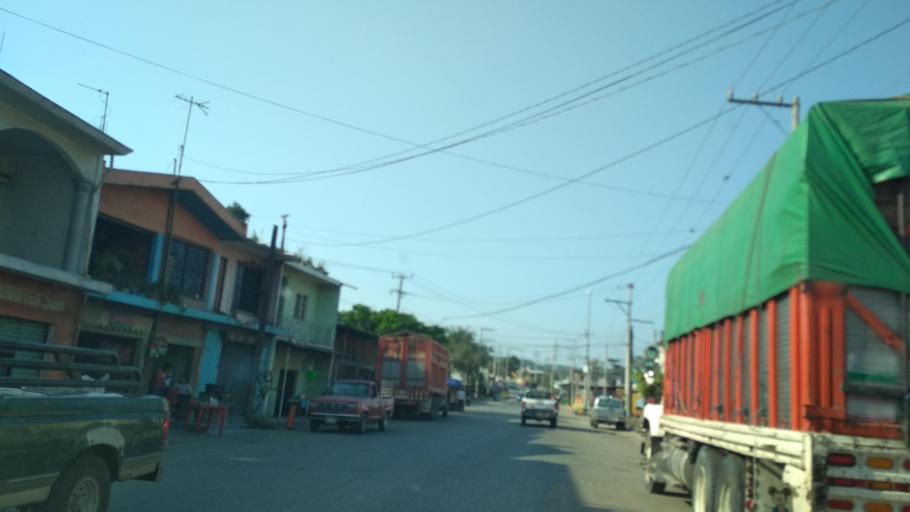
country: MM
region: Shan
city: Taunggyi
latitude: 20.3993
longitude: 97.3357
